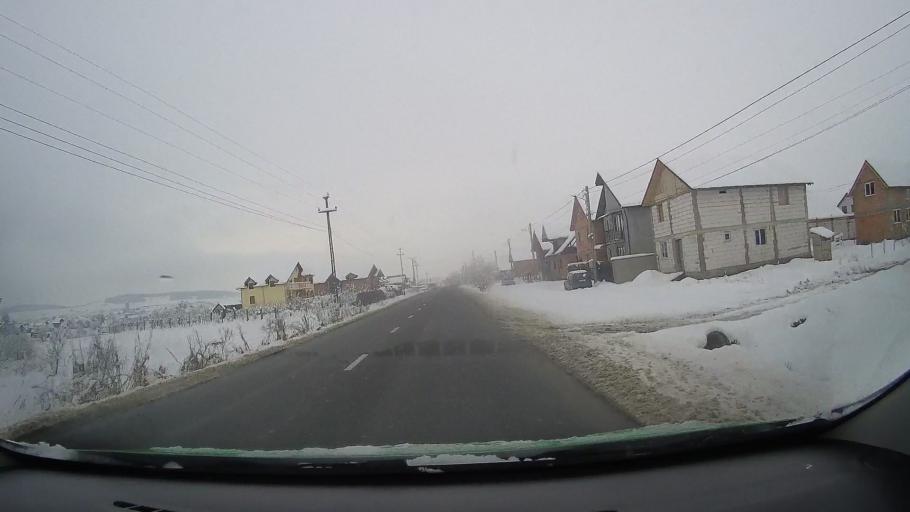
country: RO
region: Sibiu
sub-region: Comuna Cristian
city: Cristian
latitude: 45.7731
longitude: 24.0212
